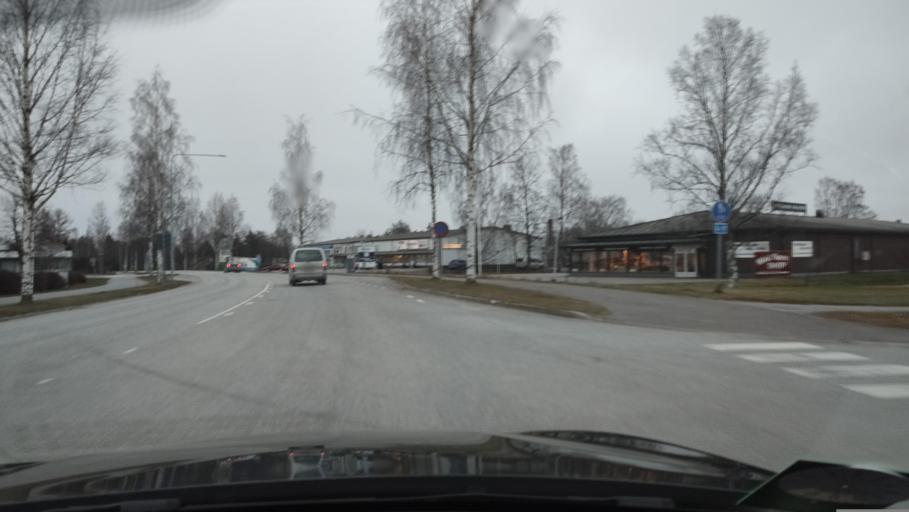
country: FI
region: Southern Ostrobothnia
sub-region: Suupohja
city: Kauhajoki
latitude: 62.4341
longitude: 22.1844
